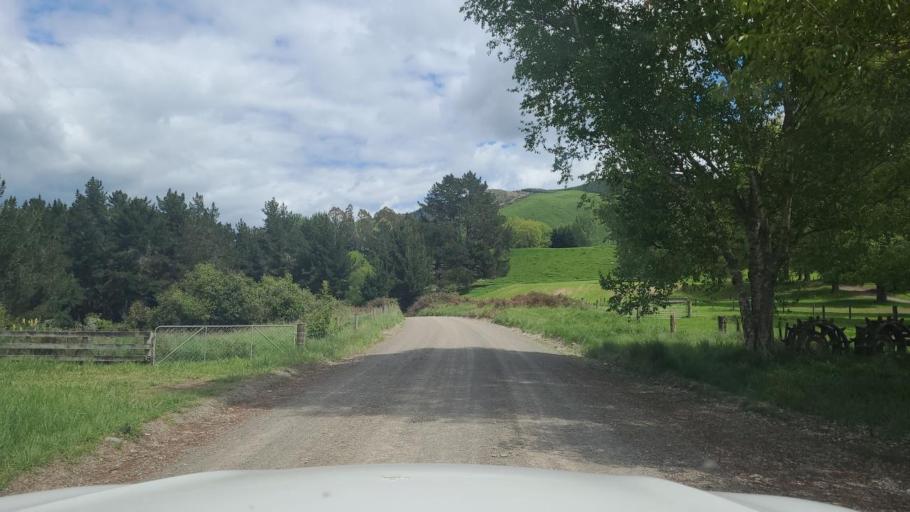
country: NZ
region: Hawke's Bay
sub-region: Napier City
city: Taradale
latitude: -39.1874
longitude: 176.6276
